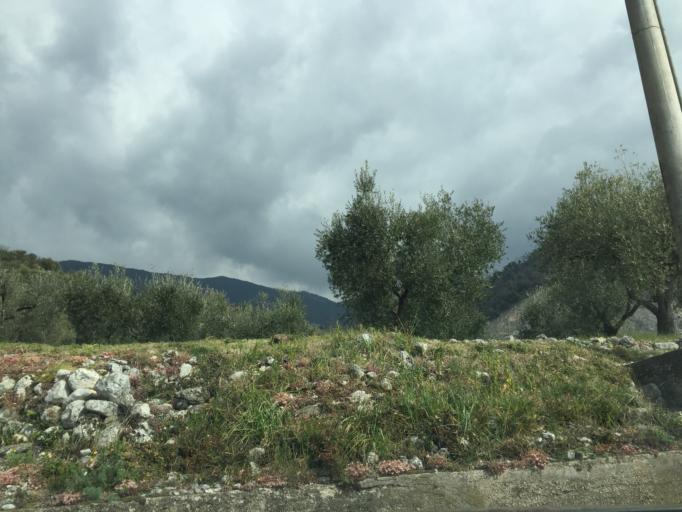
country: IT
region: Latium
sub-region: Provincia di Frosinone
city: Castrocielo
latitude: 41.5262
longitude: 13.7023
